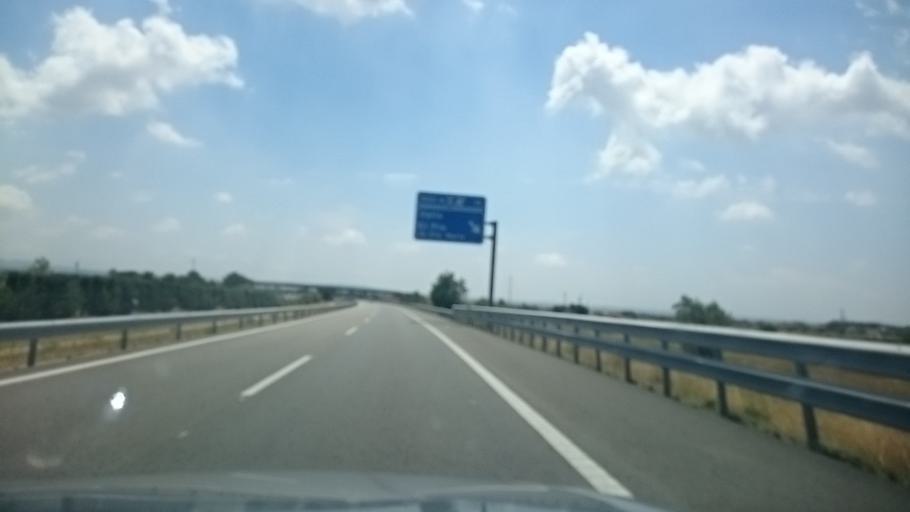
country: ES
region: Catalonia
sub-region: Provincia de Tarragona
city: El Pla de Santa Maria
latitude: 41.3753
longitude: 1.2967
